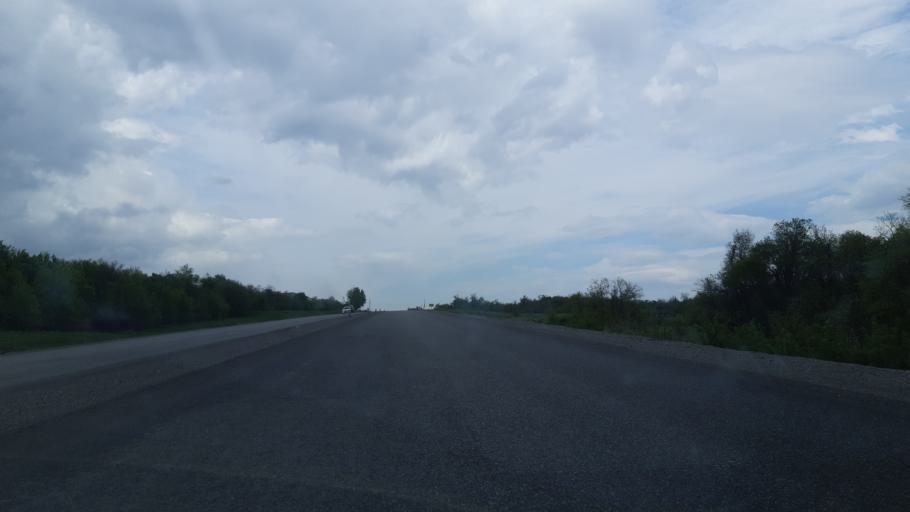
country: KZ
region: Ongtustik Qazaqstan
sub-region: Tulkibas Audany
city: Zhabagly
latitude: 42.5312
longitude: 70.6020
